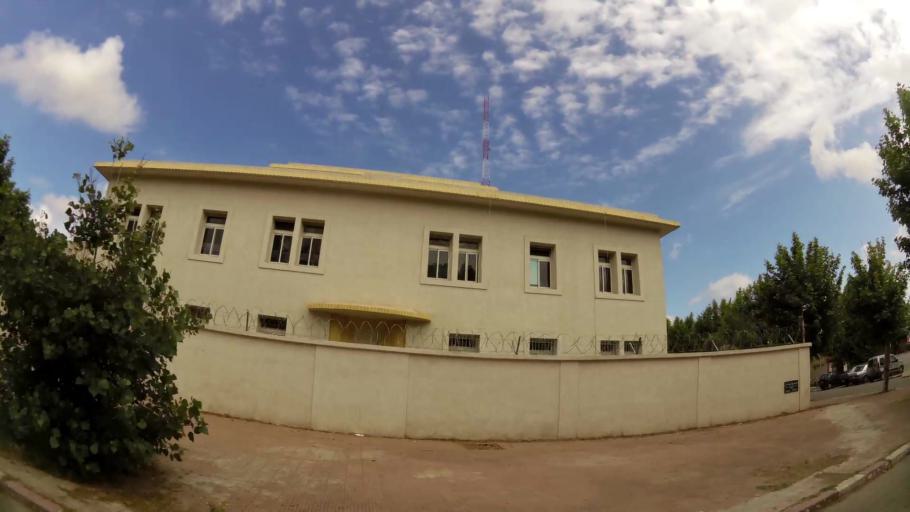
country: MA
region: Gharb-Chrarda-Beni Hssen
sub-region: Kenitra Province
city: Kenitra
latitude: 34.2528
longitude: -6.5853
